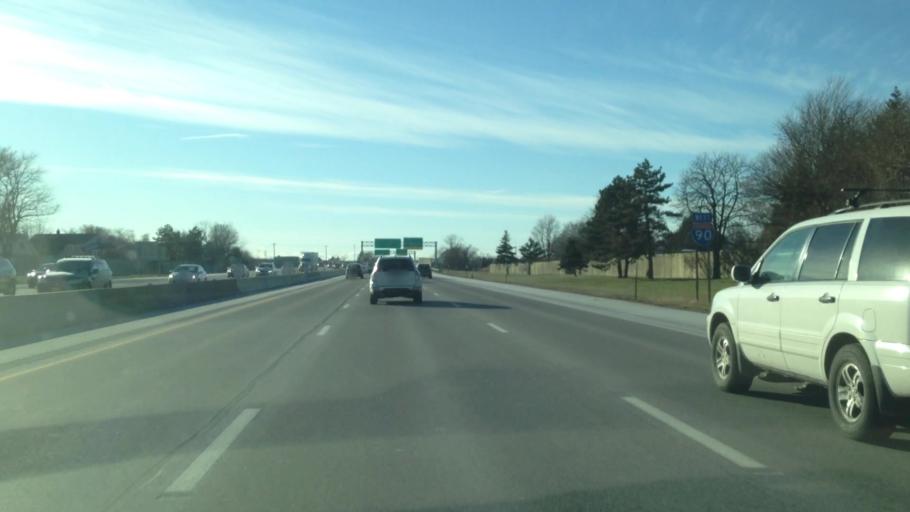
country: US
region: New York
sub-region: Erie County
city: Sloan
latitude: 42.8779
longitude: -78.7791
